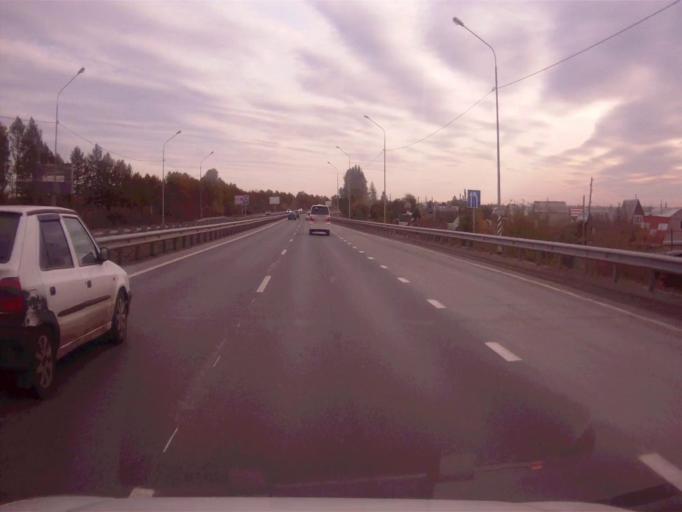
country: RU
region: Chelyabinsk
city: Novosineglazovskiy
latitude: 55.0301
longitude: 61.4470
